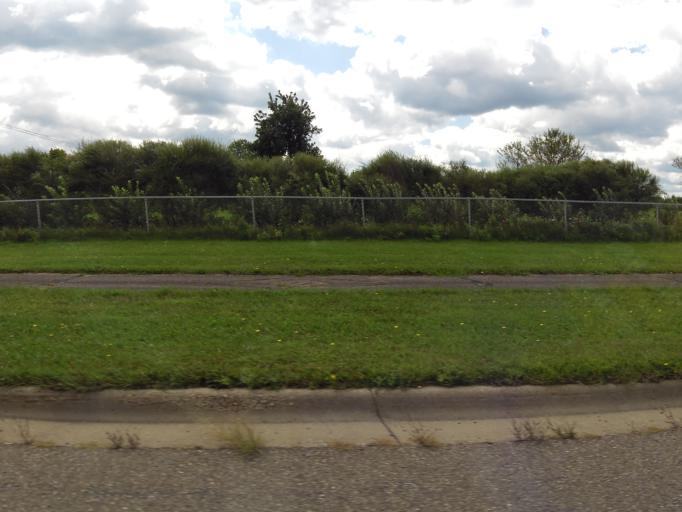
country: US
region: Minnesota
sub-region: Dakota County
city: Apple Valley
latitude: 44.7174
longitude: -93.2492
